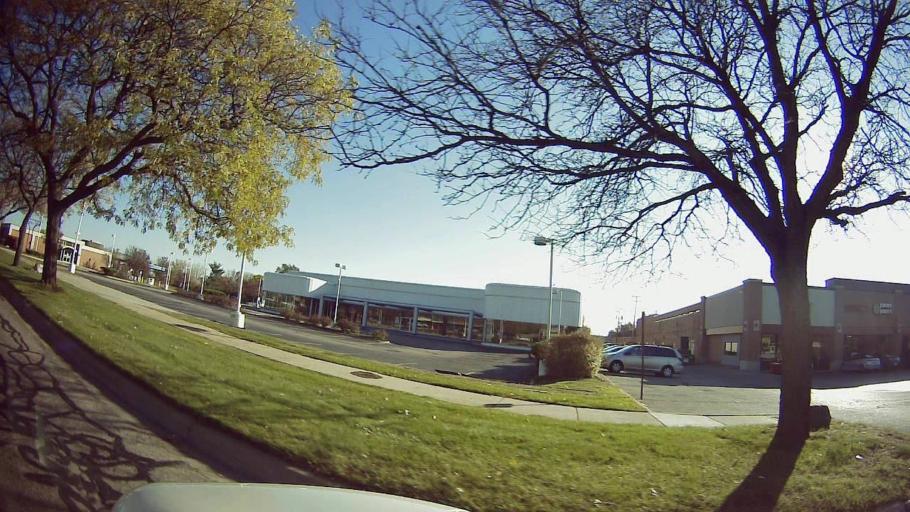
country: US
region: Michigan
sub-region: Oakland County
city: Bingham Farms
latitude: 42.5448
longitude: -83.2836
